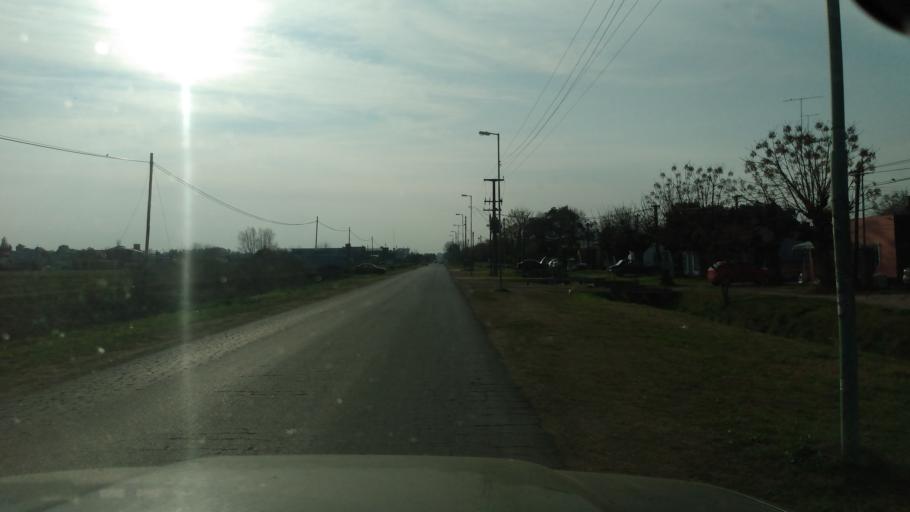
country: AR
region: Buenos Aires
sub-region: Partido de Lujan
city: Lujan
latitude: -34.5809
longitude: -59.1793
